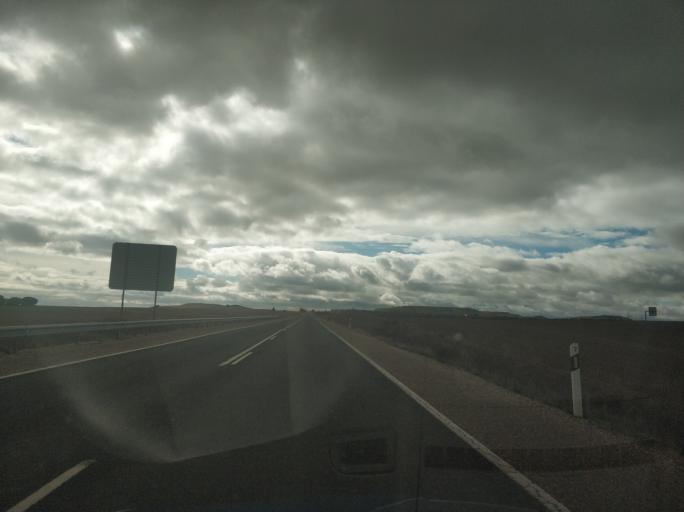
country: ES
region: Castille and Leon
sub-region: Provincia de Zamora
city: Castrillo de la Guarena
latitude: 41.2226
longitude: -5.3152
